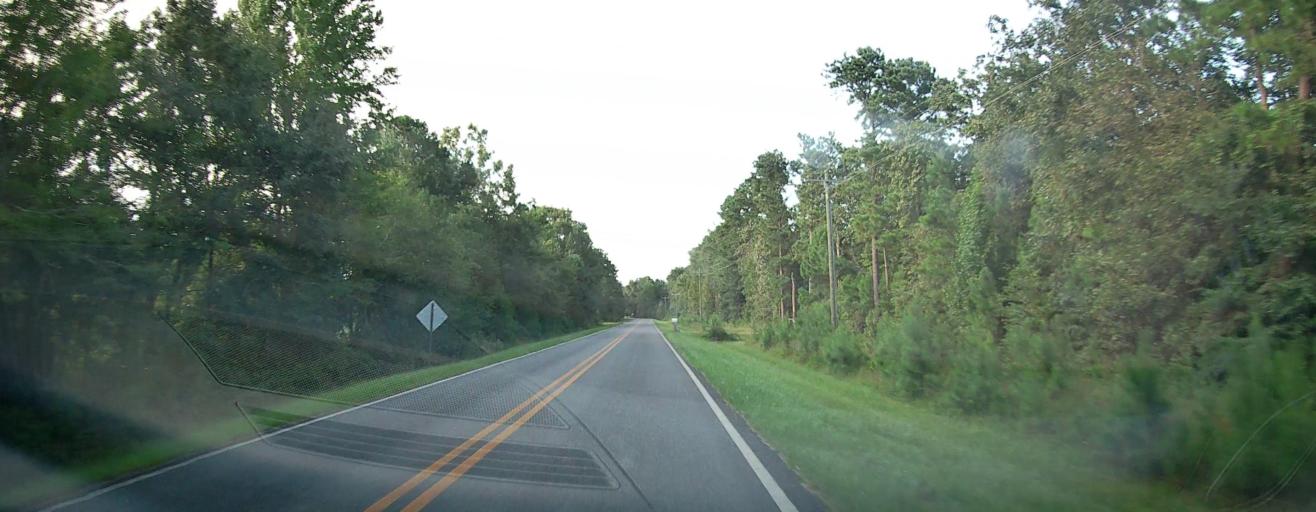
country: US
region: Georgia
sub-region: Pulaski County
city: Hawkinsville
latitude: 32.2903
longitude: -83.5531
